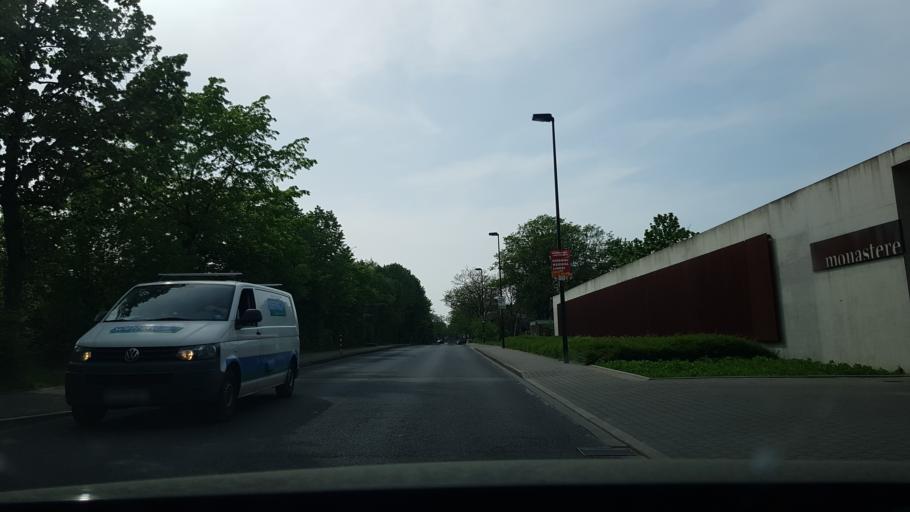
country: DE
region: North Rhine-Westphalia
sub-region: Regierungsbezirk Dusseldorf
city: Dusseldorf
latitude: 51.2632
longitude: 6.7858
